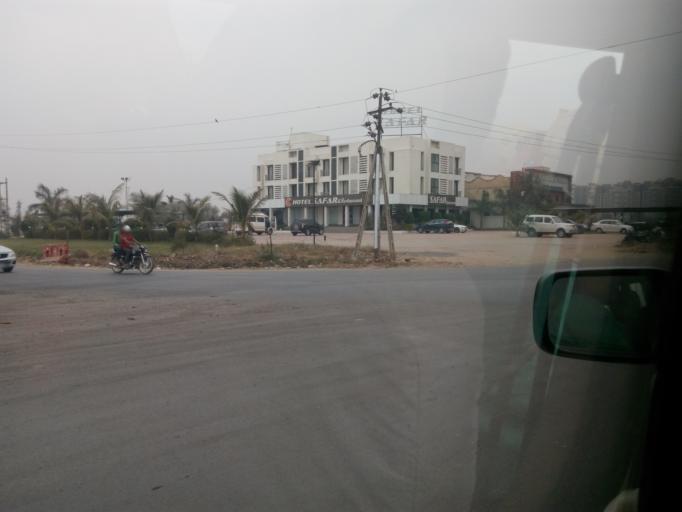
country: IN
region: Gujarat
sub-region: Ahmadabad
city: Sarkhej
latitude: 22.9892
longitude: 72.4712
